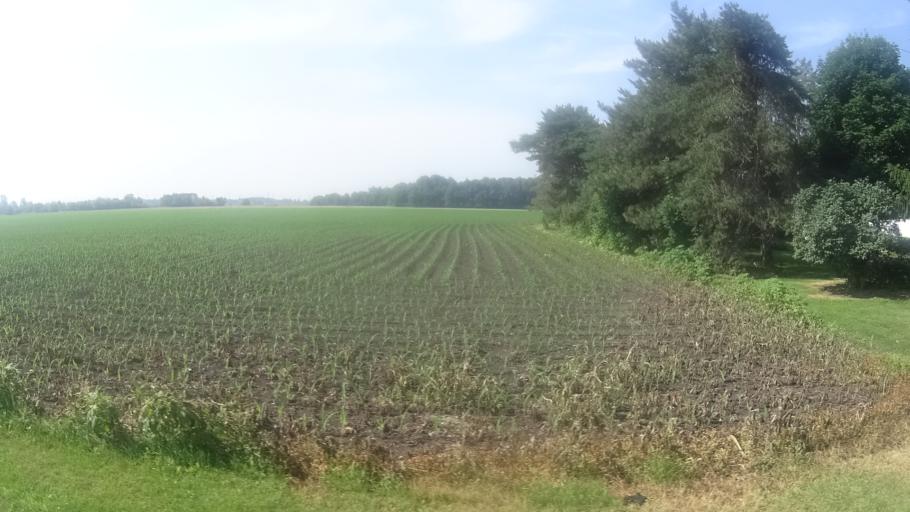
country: US
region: Ohio
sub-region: Huron County
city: Bellevue
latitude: 41.2947
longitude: -82.8081
